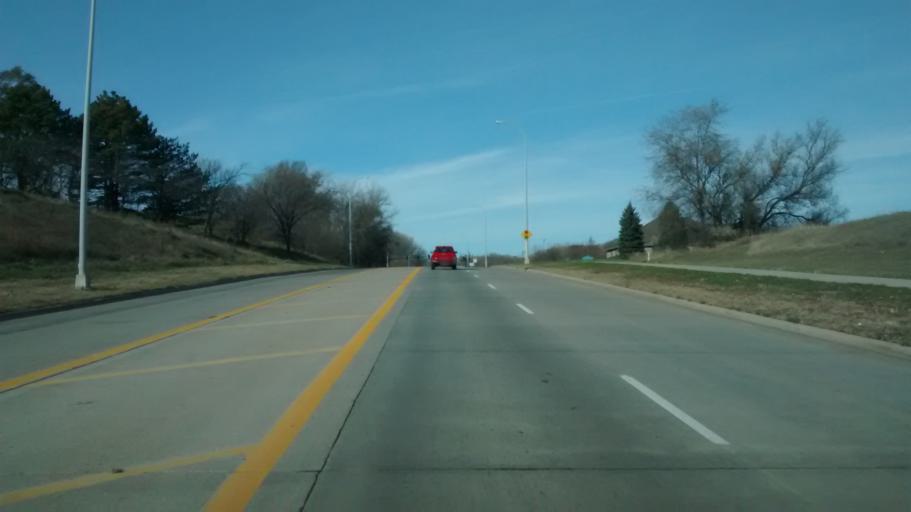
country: US
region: Iowa
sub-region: Woodbury County
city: Sioux City
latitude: 42.5350
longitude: -96.3718
